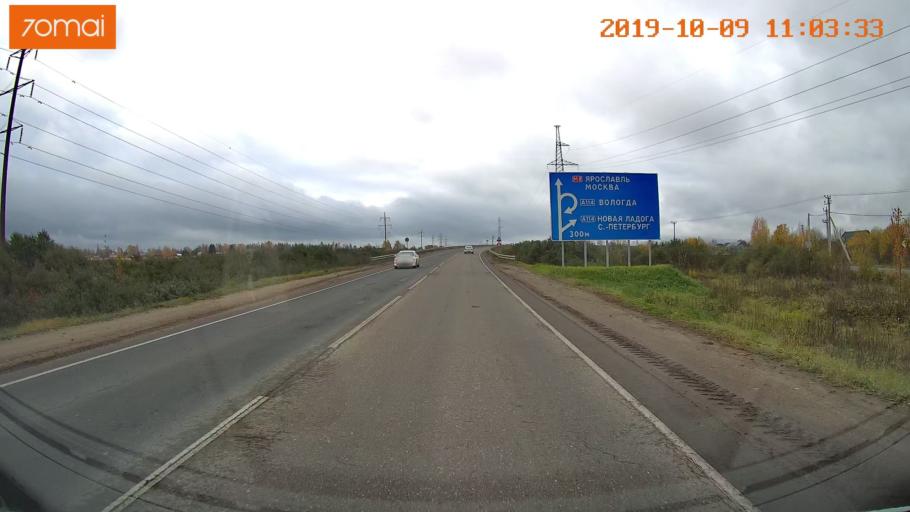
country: RU
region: Vologda
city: Vologda
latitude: 59.2208
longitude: 39.7741
